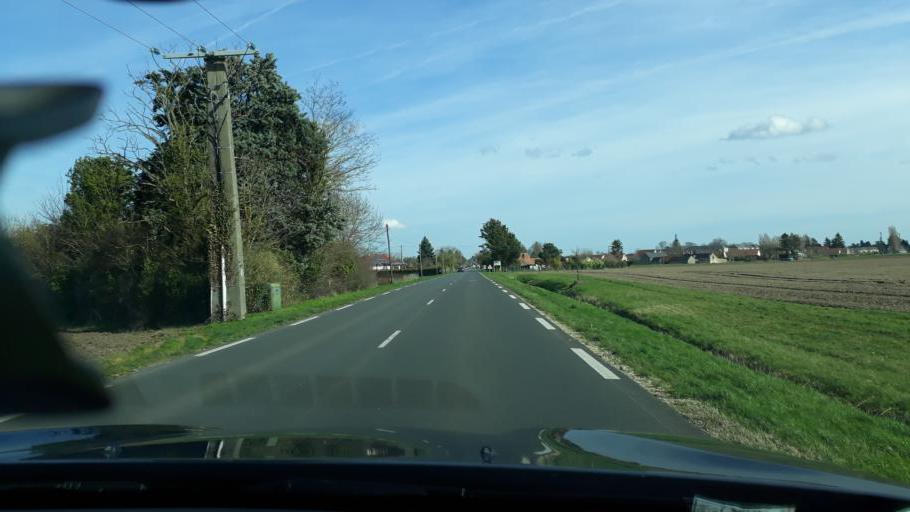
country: FR
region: Centre
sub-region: Departement du Loiret
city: Neuville-aux-Bois
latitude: 48.0681
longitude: 2.0368
